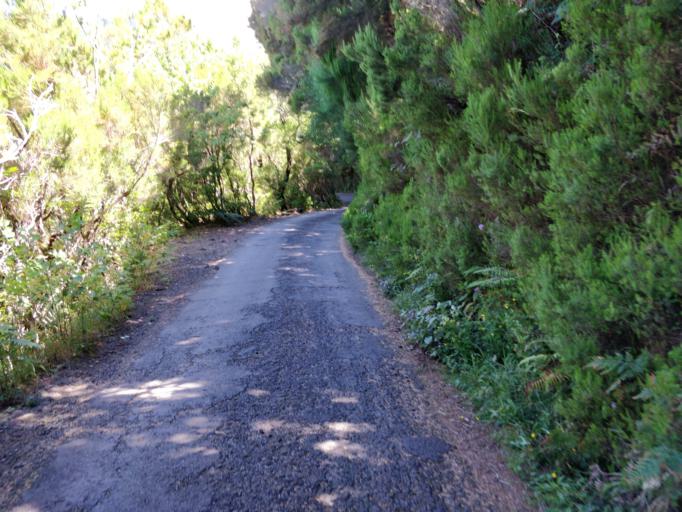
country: PT
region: Madeira
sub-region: Calheta
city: Arco da Calheta
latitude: 32.7615
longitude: -17.1334
